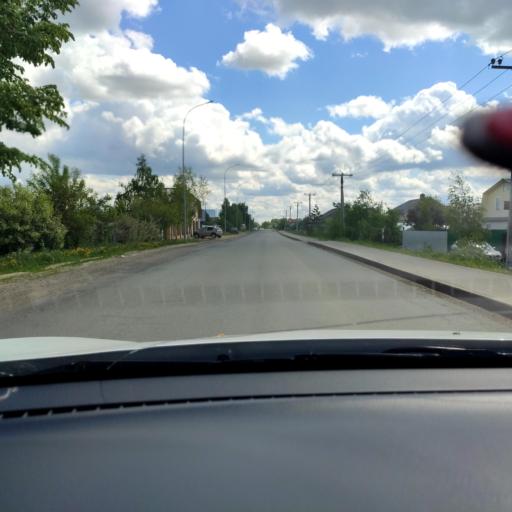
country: RU
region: Tatarstan
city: Stolbishchi
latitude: 55.6978
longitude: 49.1889
